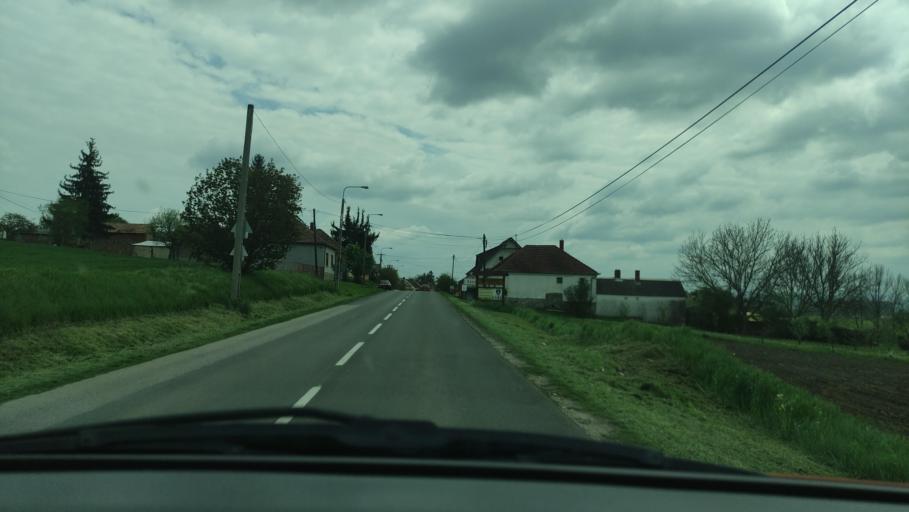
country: HU
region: Baranya
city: Sasd
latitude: 46.2603
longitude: 18.0935
